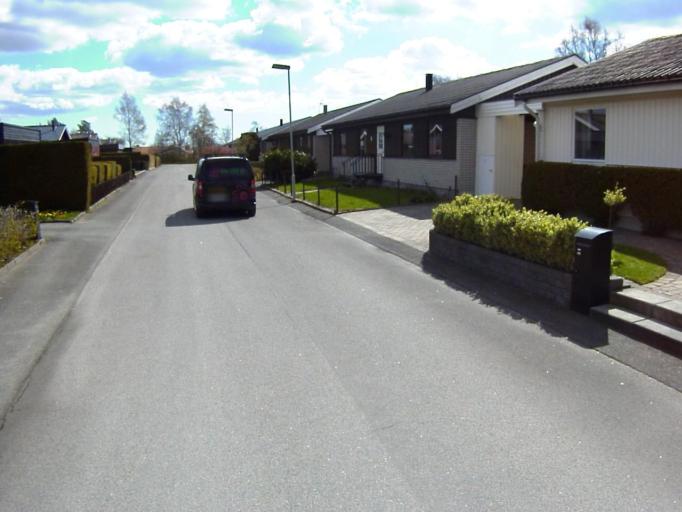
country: SE
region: Skane
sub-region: Kristianstads Kommun
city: Norra Asum
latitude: 56.0069
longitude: 14.0963
